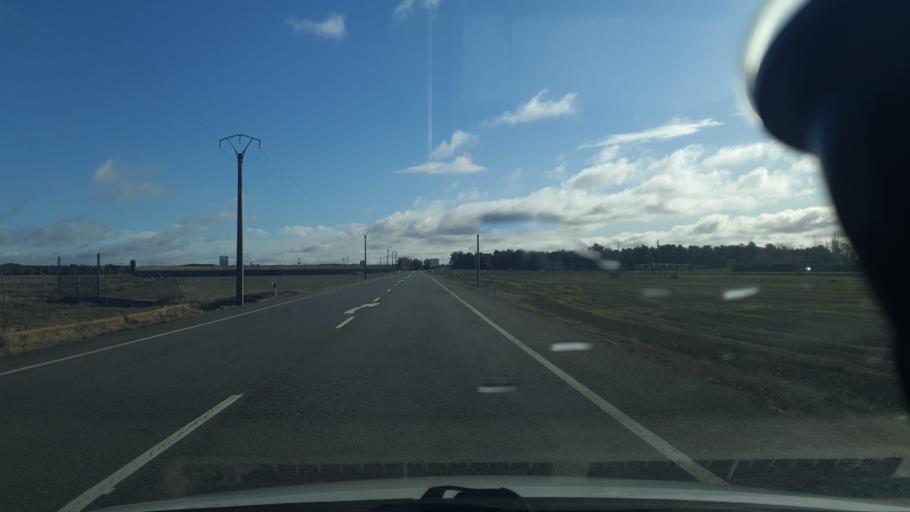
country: ES
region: Castille and Leon
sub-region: Provincia de Segovia
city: Martin Munoz de la Dehesa
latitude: 41.0471
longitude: -4.6884
